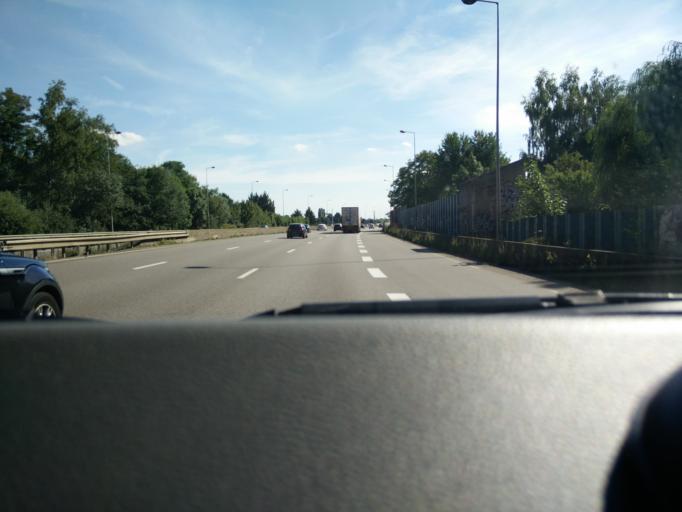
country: FR
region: Lorraine
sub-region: Departement de la Moselle
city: Talange
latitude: 49.2384
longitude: 6.1808
